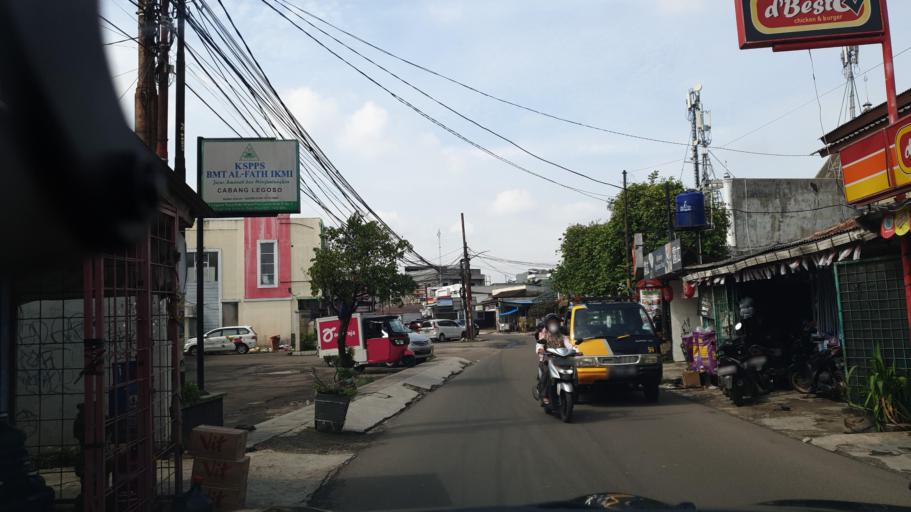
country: ID
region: West Java
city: Pamulang
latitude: -6.3159
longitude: 106.7539
